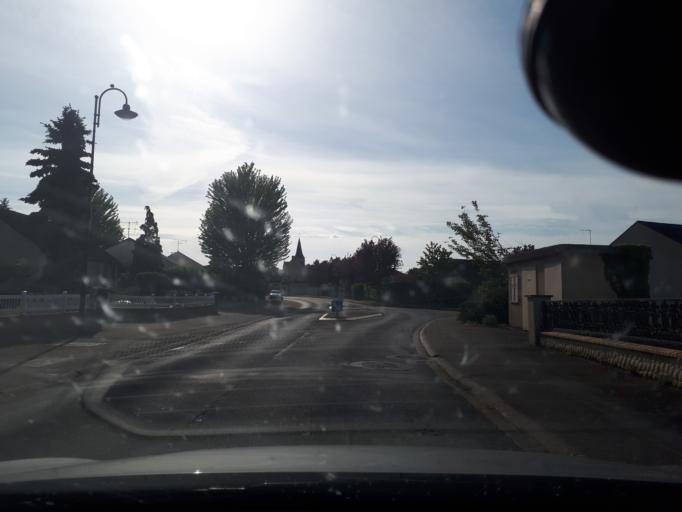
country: FR
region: Pays de la Loire
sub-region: Departement de la Sarthe
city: Saint-Mars-la-Briere
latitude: 48.0665
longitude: 0.3469
